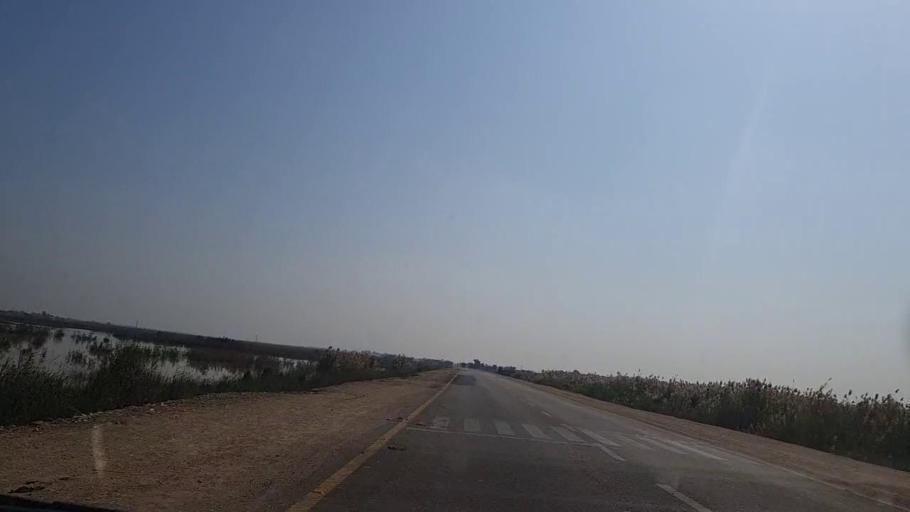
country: PK
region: Sindh
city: Sakrand
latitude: 26.0801
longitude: 68.4029
